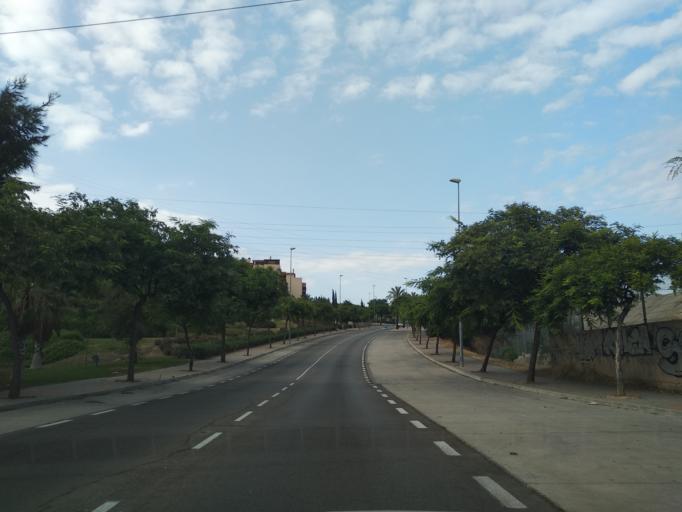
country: ES
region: Andalusia
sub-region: Provincia de Malaga
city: Malaga
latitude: 36.7279
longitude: -4.4745
